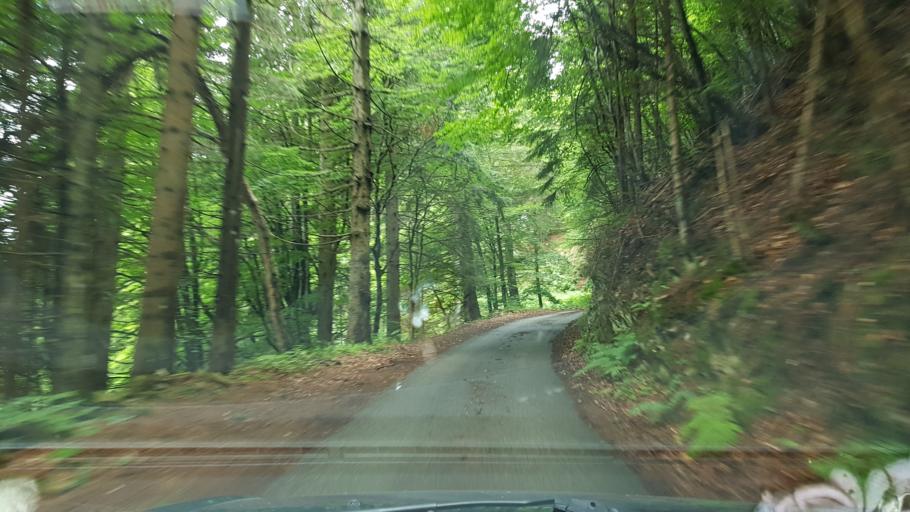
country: IT
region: Friuli Venezia Giulia
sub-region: Provincia di Udine
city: Cercivento
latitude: 46.5420
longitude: 12.9888
